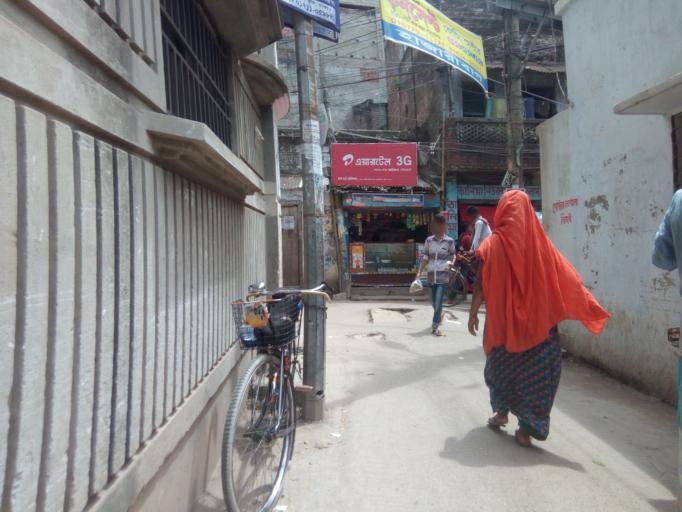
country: BD
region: Dhaka
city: Azimpur
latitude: 23.7272
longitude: 90.3727
